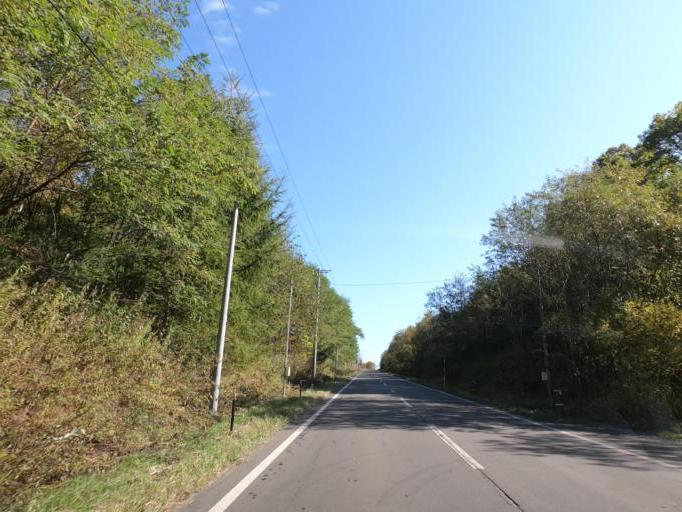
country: JP
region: Hokkaido
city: Otofuke
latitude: 42.9964
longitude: 143.2611
